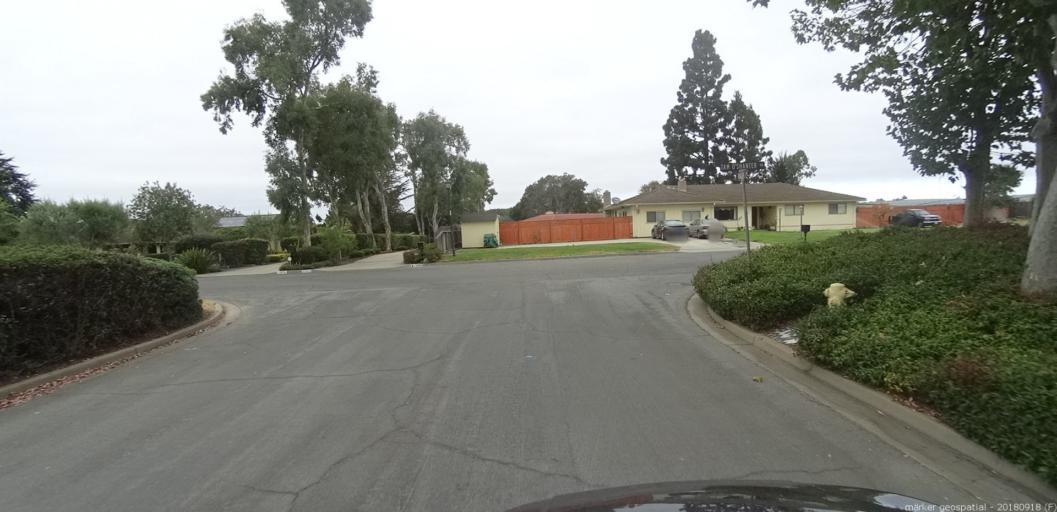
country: US
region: California
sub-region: Monterey County
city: Prunedale
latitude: 36.7483
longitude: -121.6284
